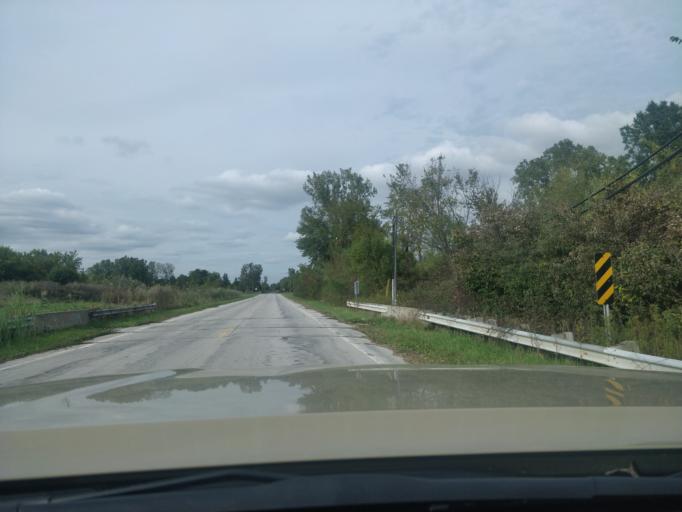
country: US
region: Michigan
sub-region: Wayne County
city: Romulus
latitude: 42.1687
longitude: -83.3642
